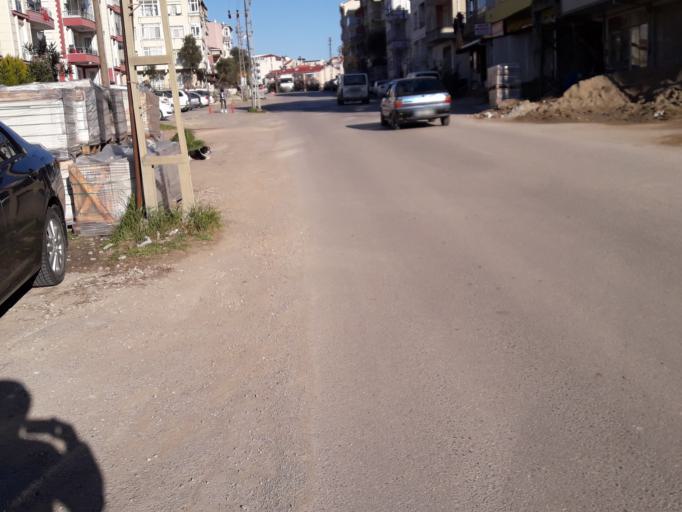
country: TR
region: Sinop
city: Sinop
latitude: 42.0225
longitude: 35.1303
